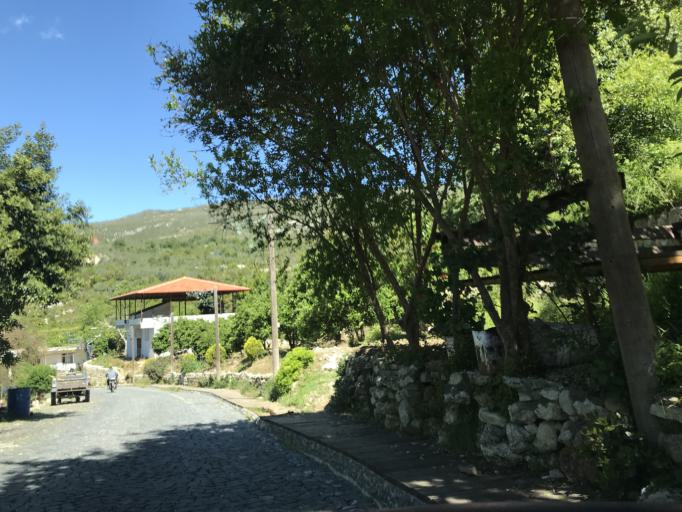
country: TR
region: Hatay
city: Samandag
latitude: 36.1324
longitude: 35.9759
